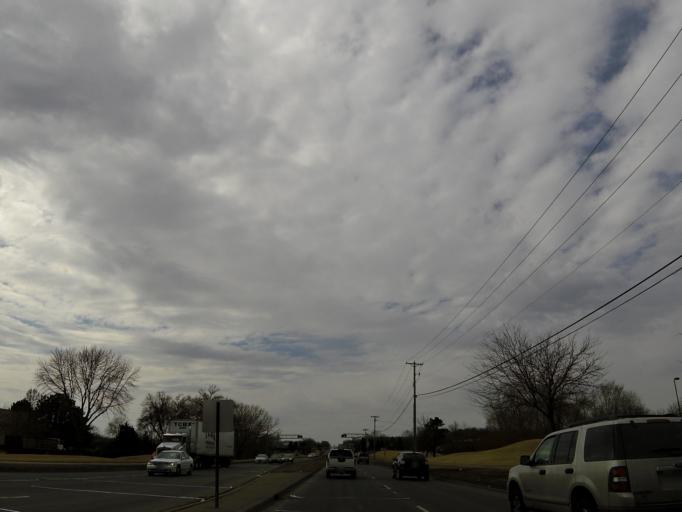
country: US
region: Minnesota
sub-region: Scott County
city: Savage
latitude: 44.8080
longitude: -93.3638
